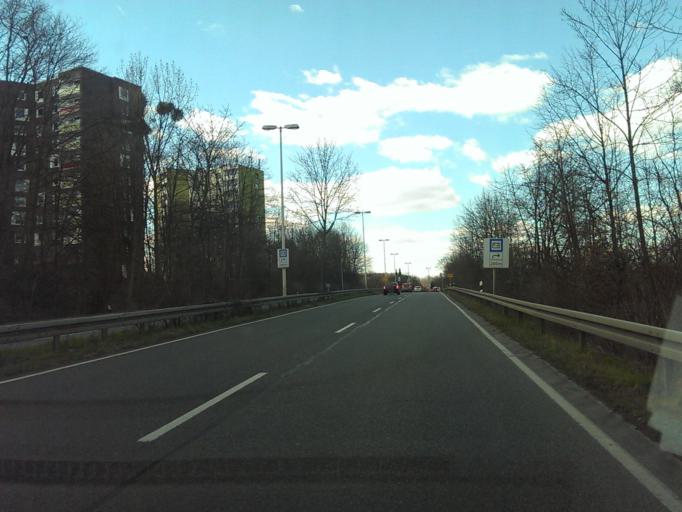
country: DE
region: Lower Saxony
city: Hildesheim
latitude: 52.1355
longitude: 9.9453
